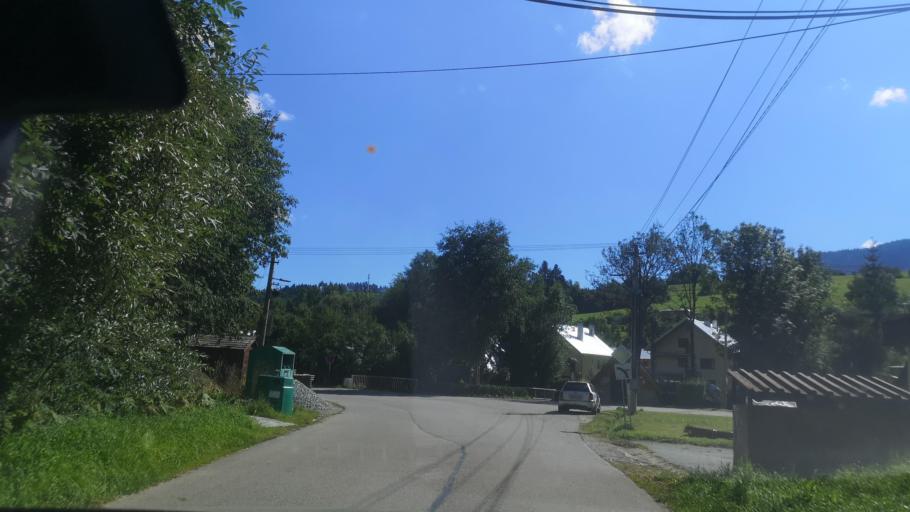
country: SK
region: Zilinsky
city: Oravska Lesna
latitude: 49.2769
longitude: 19.1340
